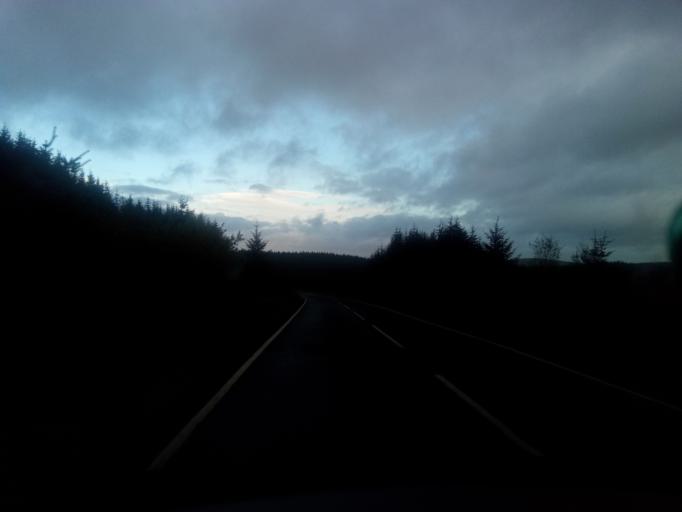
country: GB
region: Scotland
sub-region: The Scottish Borders
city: Hawick
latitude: 55.3264
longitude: -2.6467
